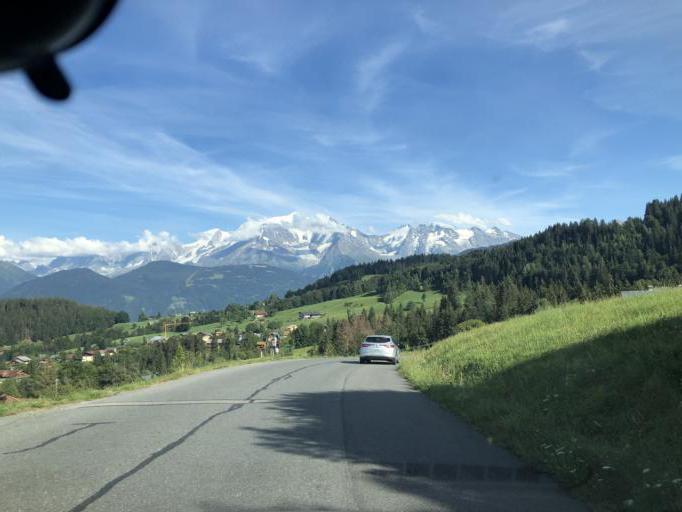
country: FR
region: Rhone-Alpes
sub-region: Departement de la Haute-Savoie
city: Cordon
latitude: 45.9152
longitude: 6.6041
